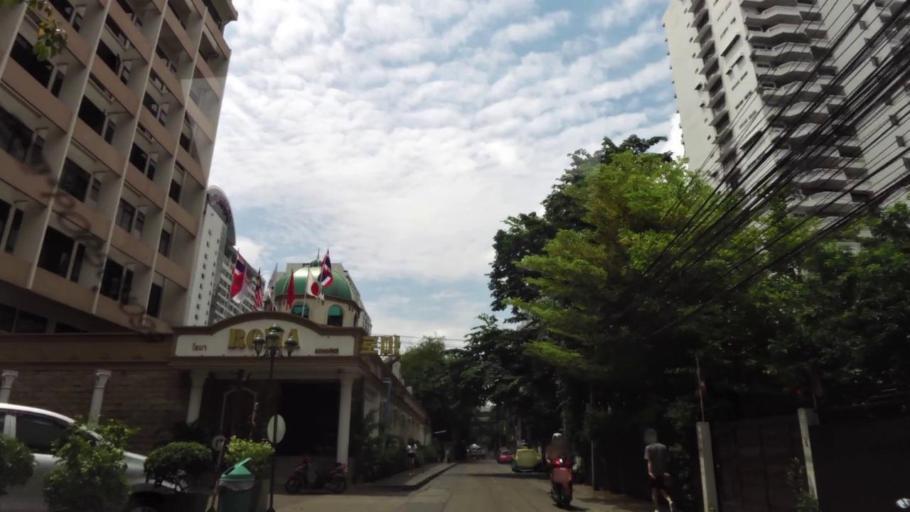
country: TH
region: Bangkok
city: Khlong Toei
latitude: 13.7396
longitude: 100.5584
